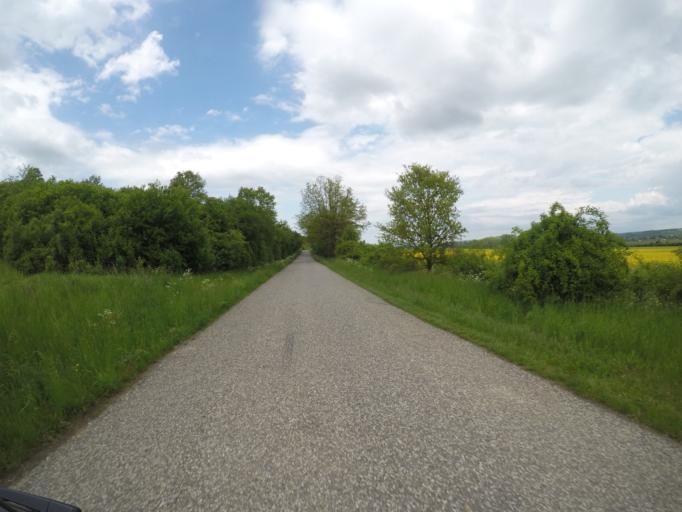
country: SK
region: Banskobystricky
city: Dudince
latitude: 48.0986
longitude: 18.8704
